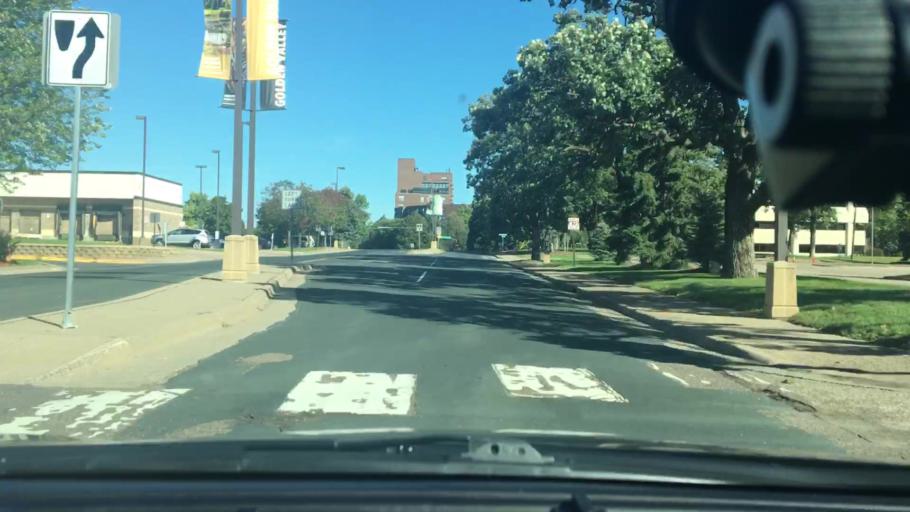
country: US
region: Minnesota
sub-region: Hennepin County
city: Golden Valley
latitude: 44.9843
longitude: -93.3772
